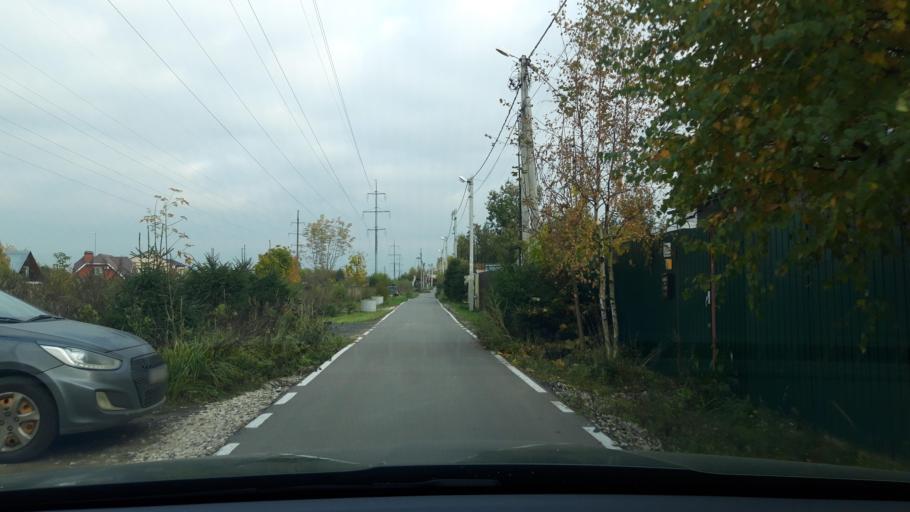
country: RU
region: Moskovskaya
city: Lozhki
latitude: 56.0622
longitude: 37.0906
